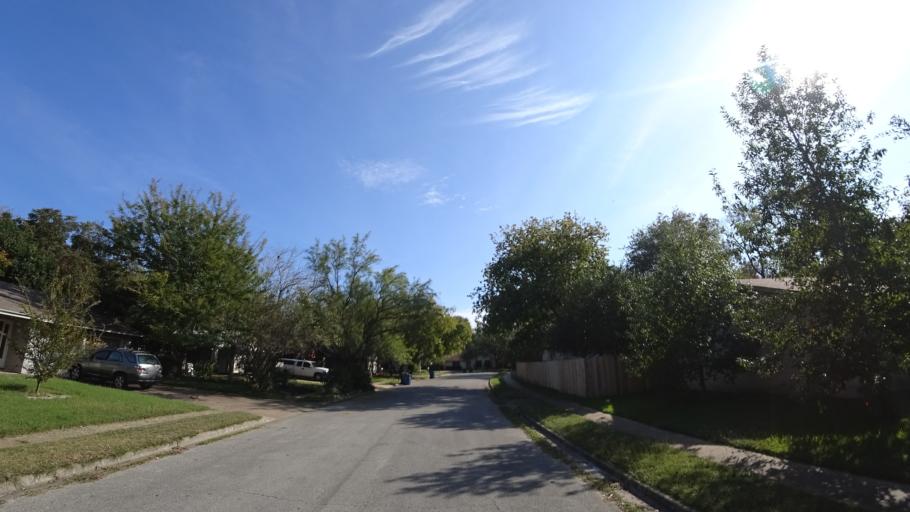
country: US
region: Texas
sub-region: Williamson County
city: Anderson Mill
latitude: 30.4540
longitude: -97.8010
